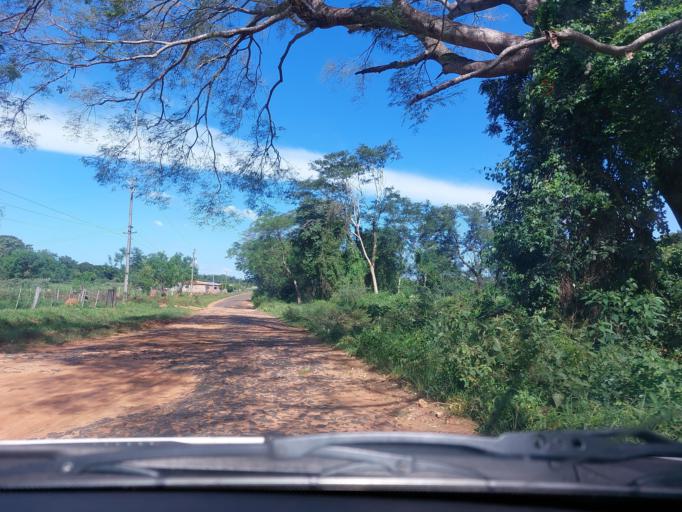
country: PY
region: San Pedro
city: Itacurubi del Rosario
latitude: -24.5808
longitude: -56.6009
